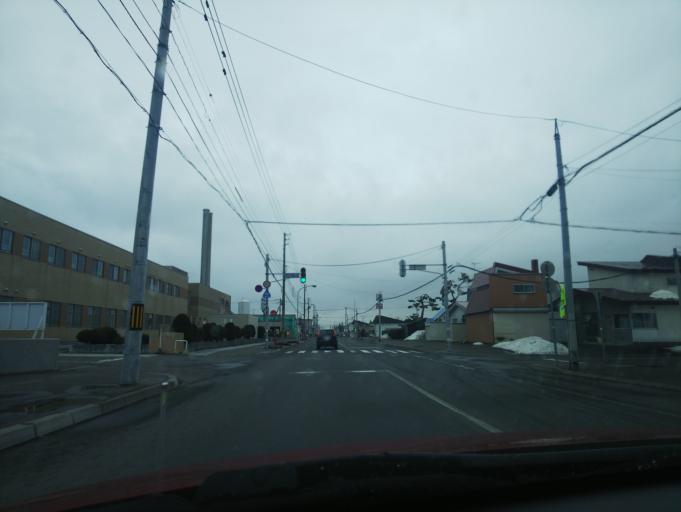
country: JP
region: Hokkaido
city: Nayoro
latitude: 44.3491
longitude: 142.4503
